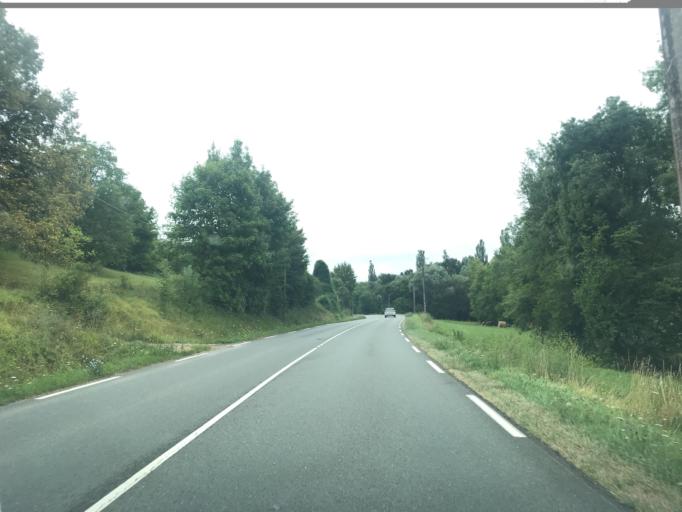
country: FR
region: Aquitaine
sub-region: Departement de la Dordogne
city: Chancelade
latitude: 45.2597
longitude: 0.6829
